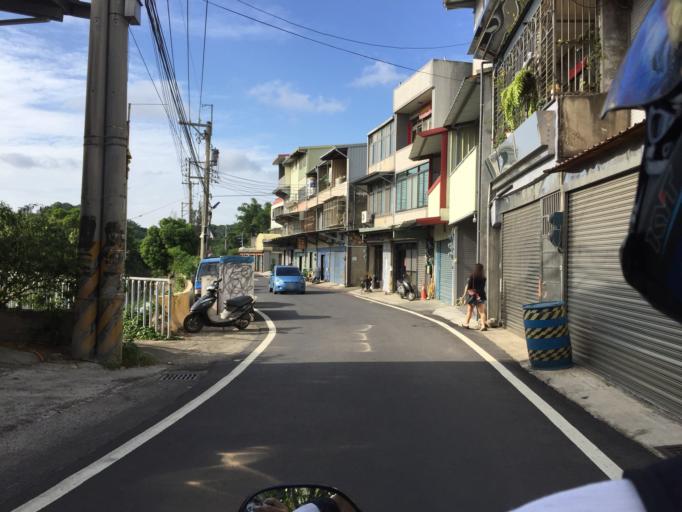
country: TW
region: Taiwan
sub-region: Hsinchu
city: Hsinchu
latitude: 24.7727
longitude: 120.9342
